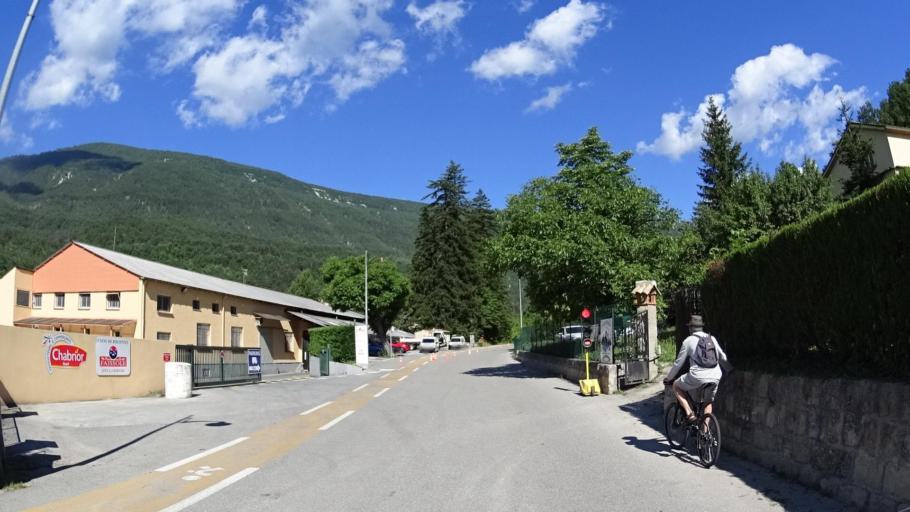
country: FR
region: Provence-Alpes-Cote d'Azur
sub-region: Departement des Alpes-de-Haute-Provence
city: Annot
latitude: 43.9691
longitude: 6.6630
